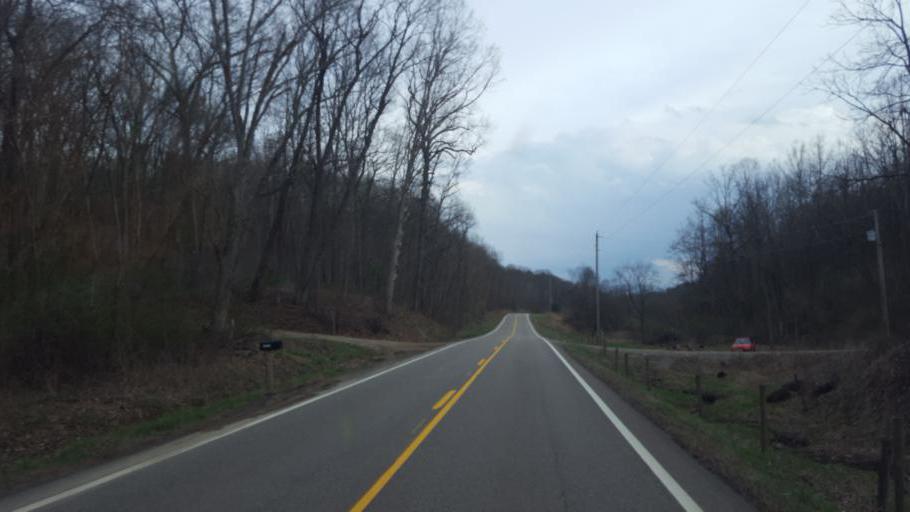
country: US
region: Ohio
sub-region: Guernsey County
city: Mantua
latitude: 40.1357
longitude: -81.7865
